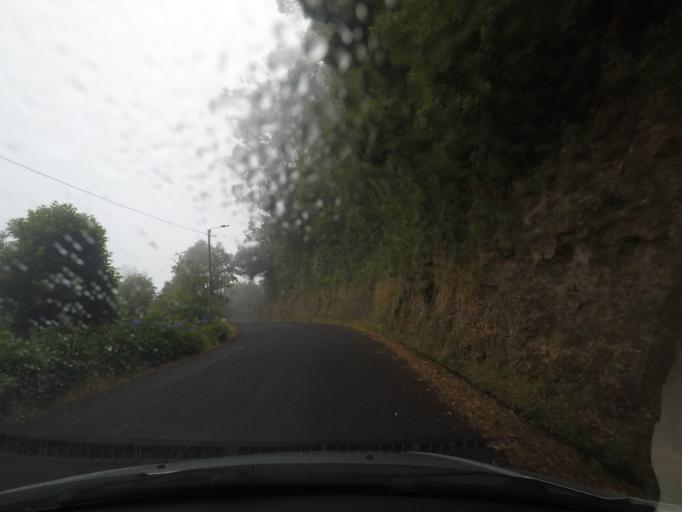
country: PT
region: Madeira
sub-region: Santana
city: Santana
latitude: 32.7473
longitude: -16.8740
